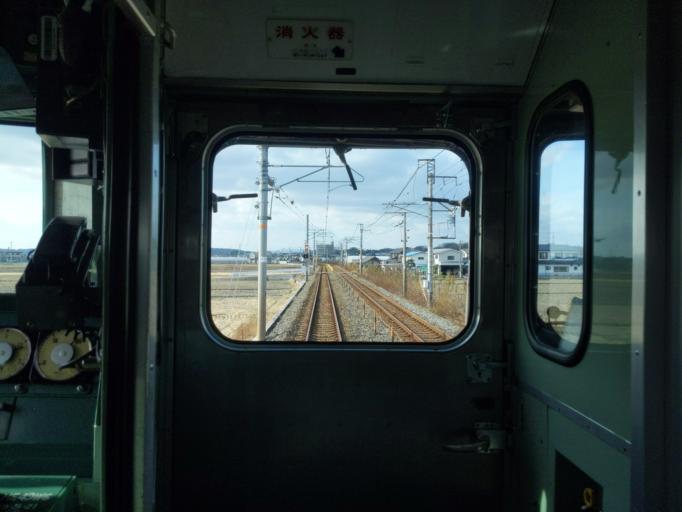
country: JP
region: Okayama
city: Kurashiki
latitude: 34.6057
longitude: 133.8519
